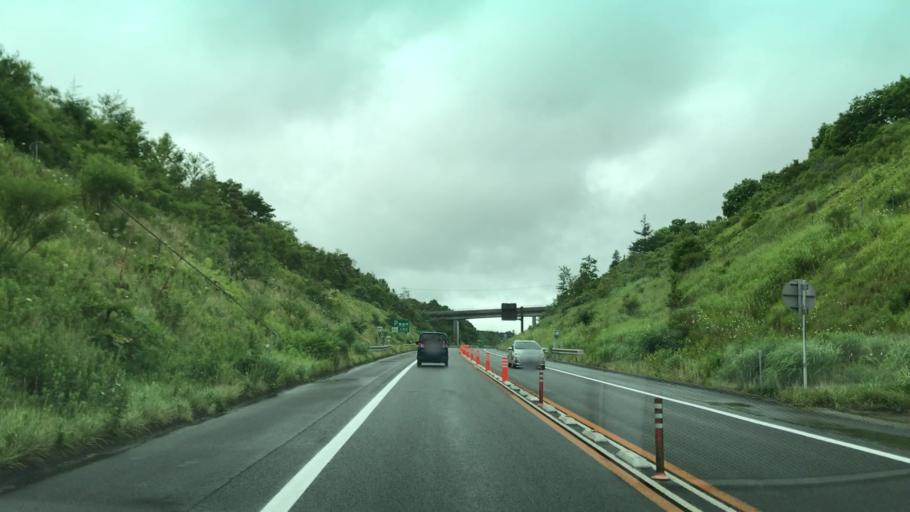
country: JP
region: Hokkaido
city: Muroran
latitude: 42.3833
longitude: 141.0039
